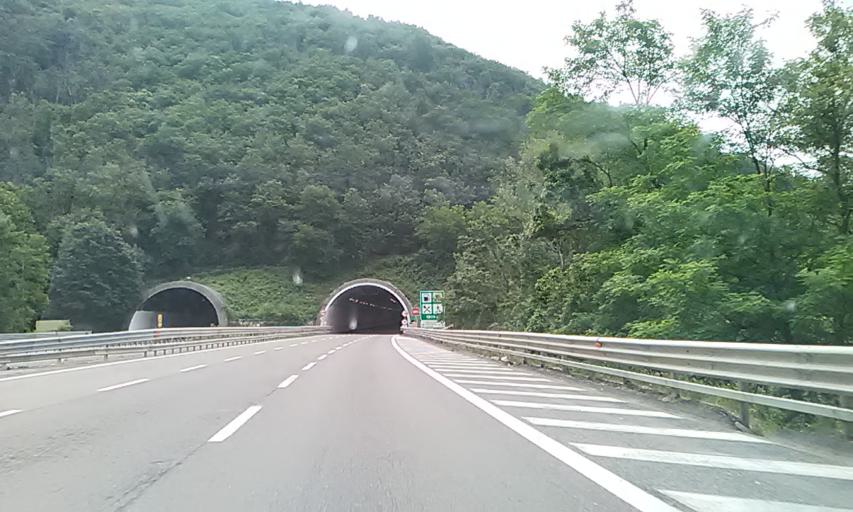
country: IT
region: Liguria
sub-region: Provincia di Genova
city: Mele
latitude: 44.4681
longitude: 8.7422
